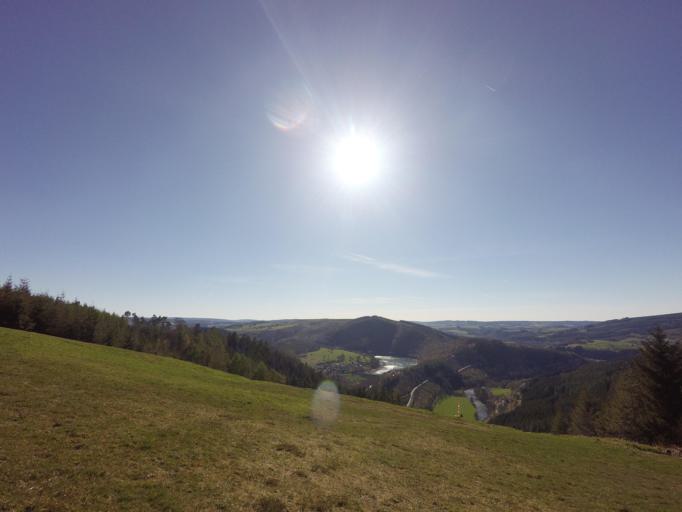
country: BE
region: Wallonia
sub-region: Province de Liege
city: Trois-Ponts
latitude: 50.3993
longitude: 5.8879
